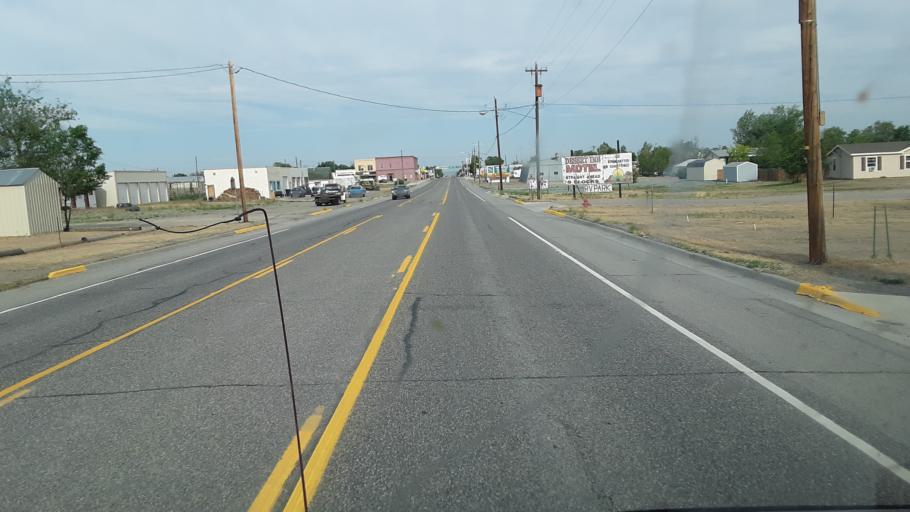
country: US
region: Wyoming
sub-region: Fremont County
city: Riverton
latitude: 43.2356
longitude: -108.1042
